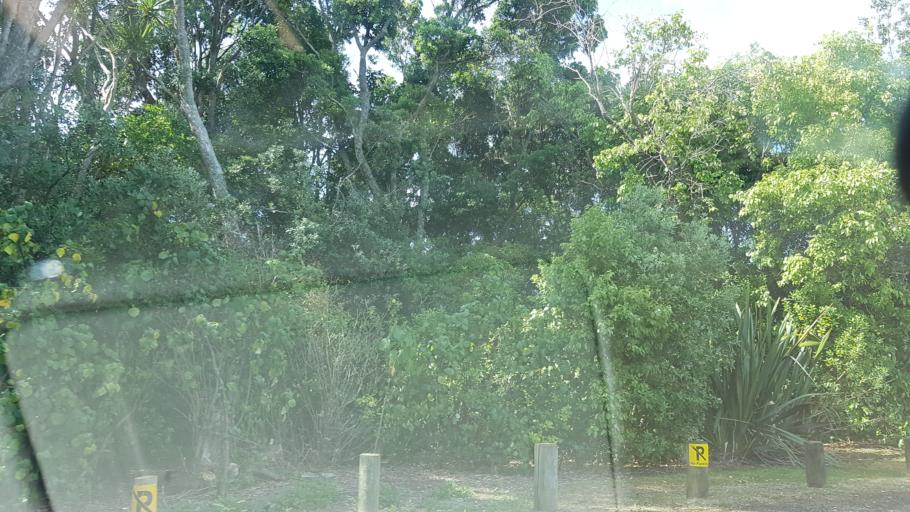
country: NZ
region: Auckland
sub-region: Auckland
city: Rothesay Bay
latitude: -36.6822
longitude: 174.7469
